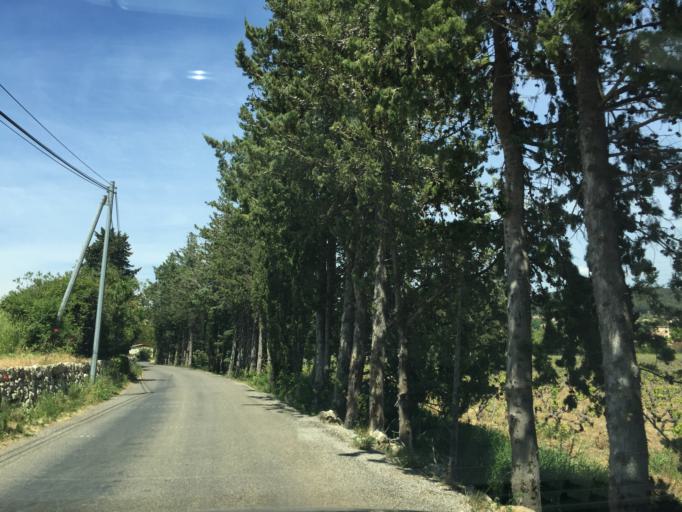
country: FR
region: Provence-Alpes-Cote d'Azur
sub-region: Departement du Var
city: Lorgues
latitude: 43.4853
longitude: 6.3634
